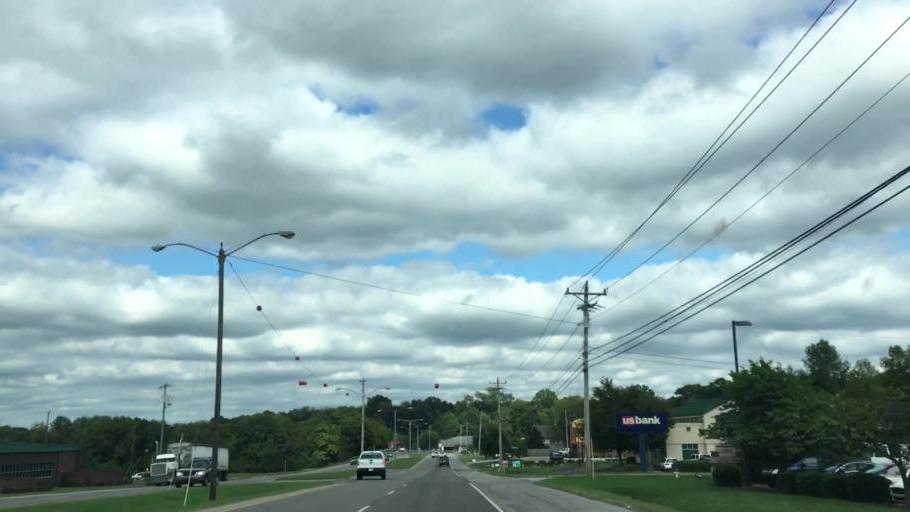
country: US
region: Tennessee
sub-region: Maury County
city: Columbia
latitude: 35.6127
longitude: -87.0676
